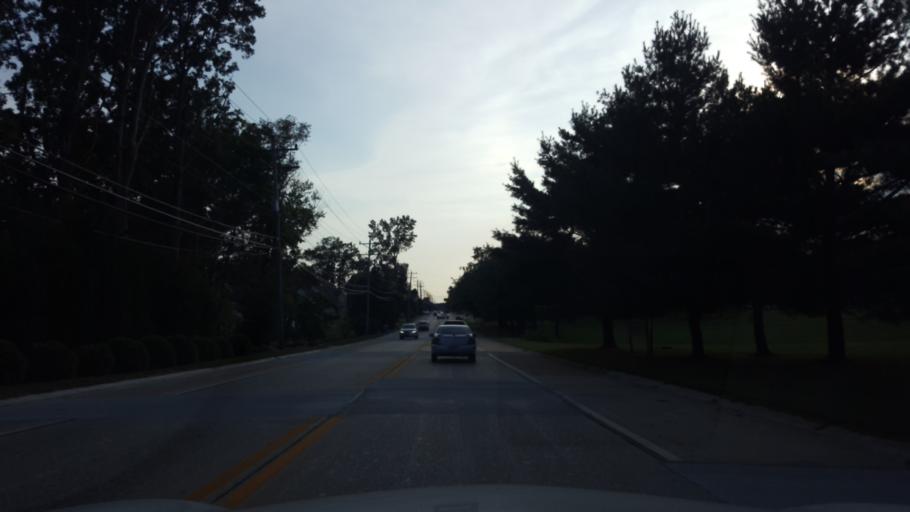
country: US
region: Delaware
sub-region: New Castle County
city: Pike Creek Valley
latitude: 39.7366
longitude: -75.6526
